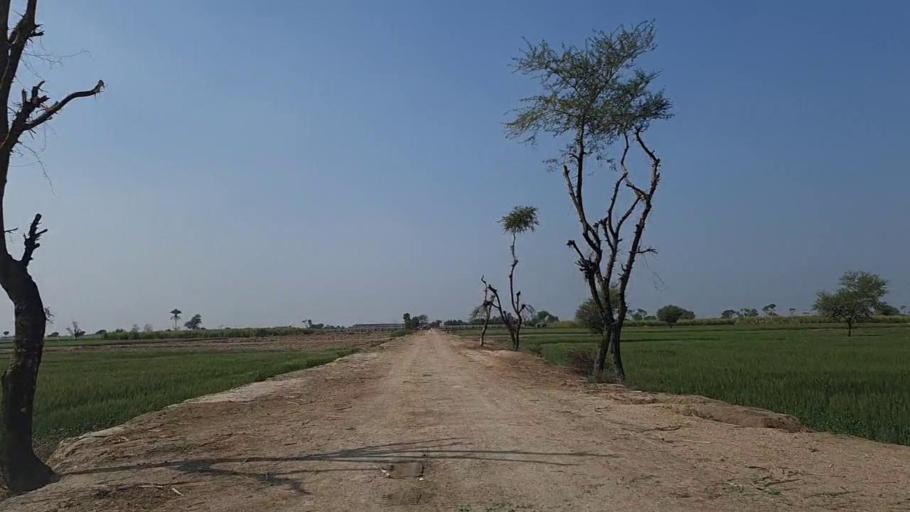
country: PK
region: Sindh
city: Nawabshah
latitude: 26.2871
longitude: 68.4895
